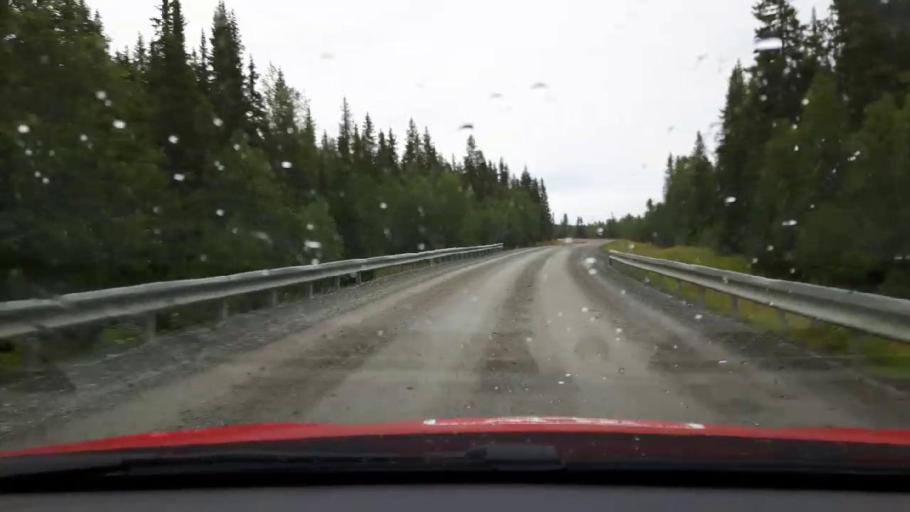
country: SE
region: Jaemtland
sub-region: Are Kommun
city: Are
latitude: 63.4707
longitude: 12.5951
